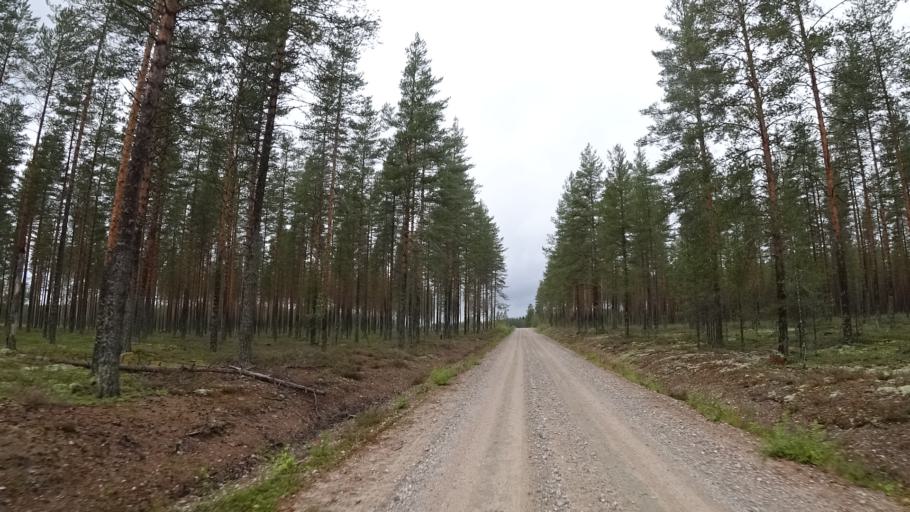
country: FI
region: North Karelia
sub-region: Pielisen Karjala
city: Lieksa
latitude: 63.5279
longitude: 30.0768
